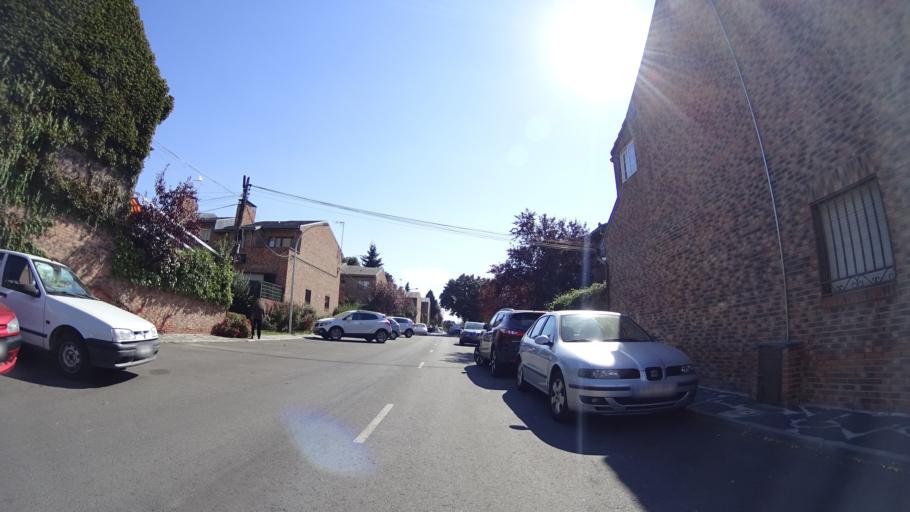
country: ES
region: Madrid
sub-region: Provincia de Madrid
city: Navalquejigo
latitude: 40.6078
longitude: -4.0323
